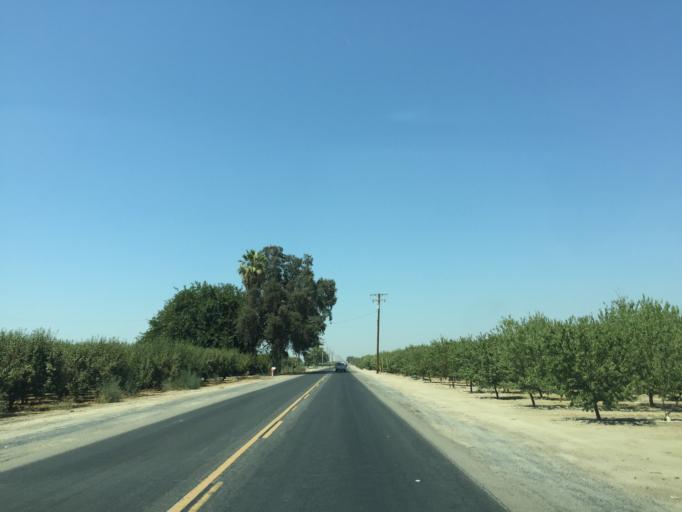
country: US
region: California
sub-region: Tulare County
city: Visalia
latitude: 36.3657
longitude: -119.3321
